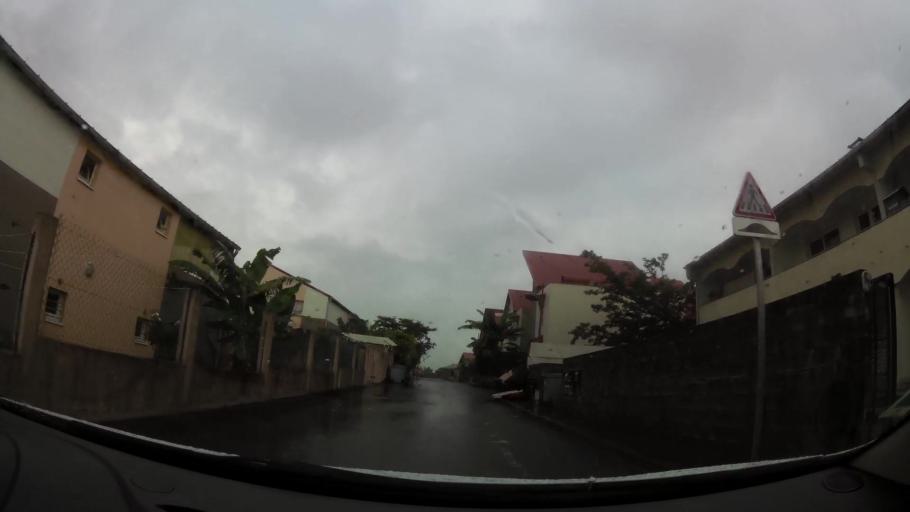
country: RE
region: Reunion
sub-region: Reunion
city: Saint-Andre
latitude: -20.9763
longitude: 55.6572
